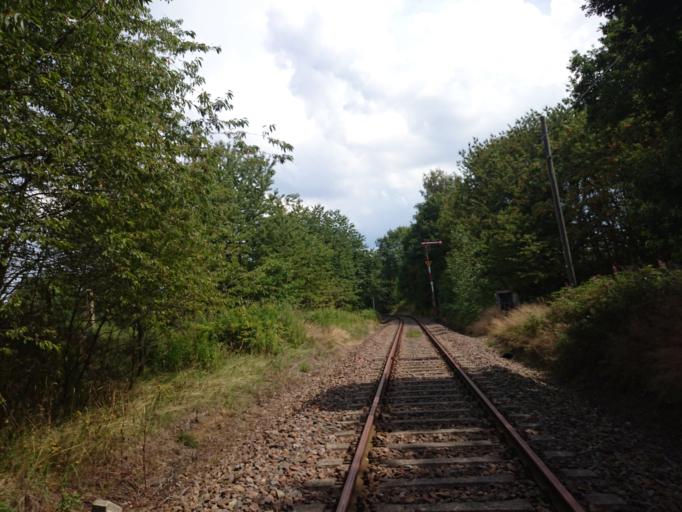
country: DE
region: Saxony
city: Brand-Erbisdorf
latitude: 50.8735
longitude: 13.3611
